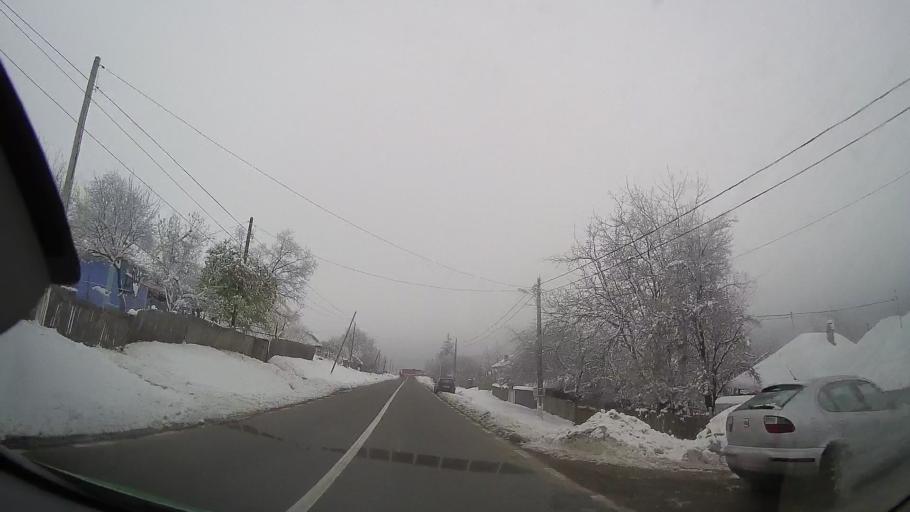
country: RO
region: Neamt
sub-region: Comuna Poenari
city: Poienari
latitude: 46.8813
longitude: 27.1319
